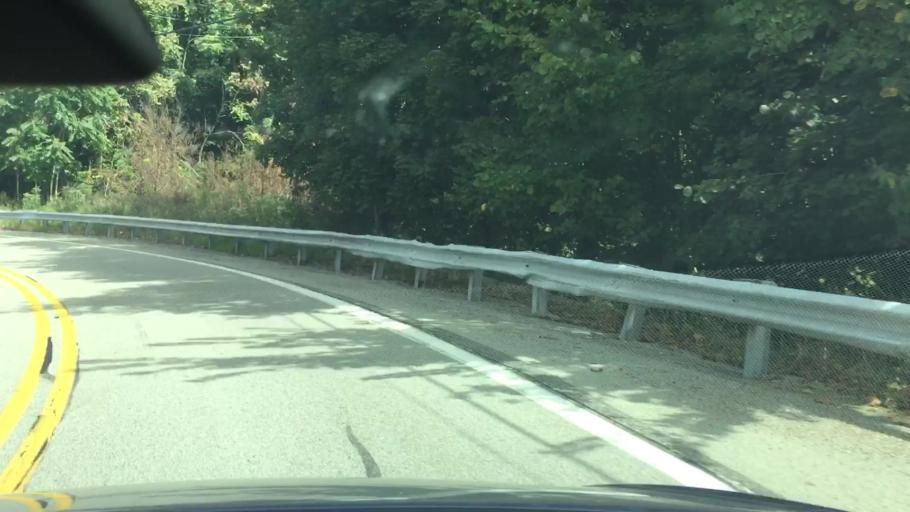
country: US
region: Pennsylvania
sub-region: Allegheny County
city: Cheswick
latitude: 40.5443
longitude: -79.8229
